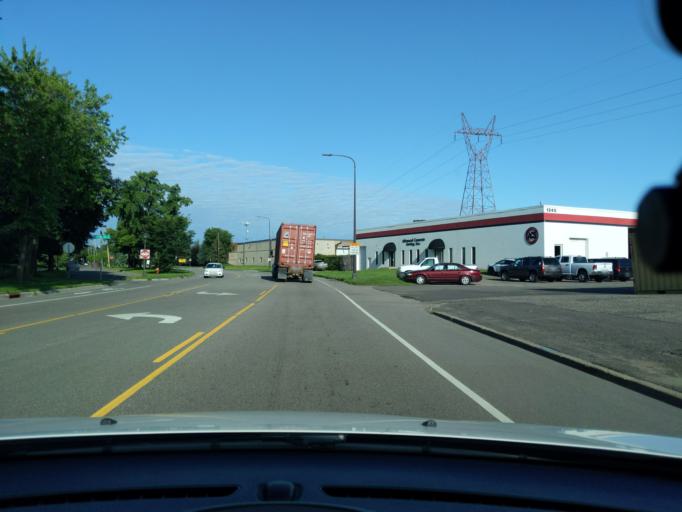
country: US
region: Minnesota
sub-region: Ramsey County
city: Falcon Heights
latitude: 44.9675
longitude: -93.1523
